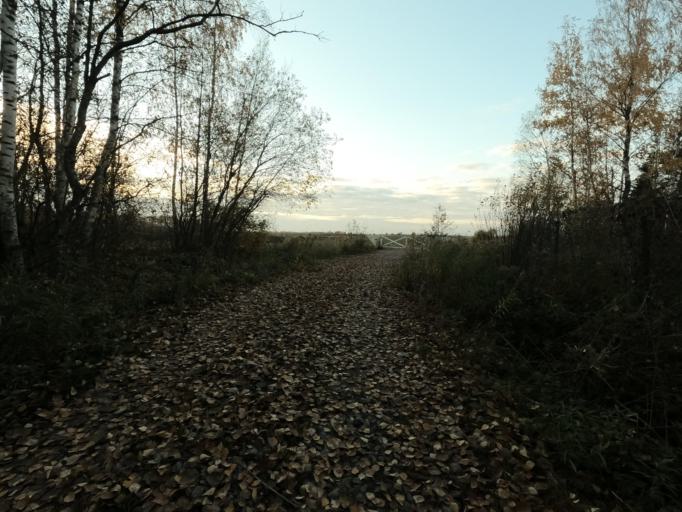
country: RU
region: Leningrad
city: Mga
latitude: 59.7828
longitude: 31.1966
